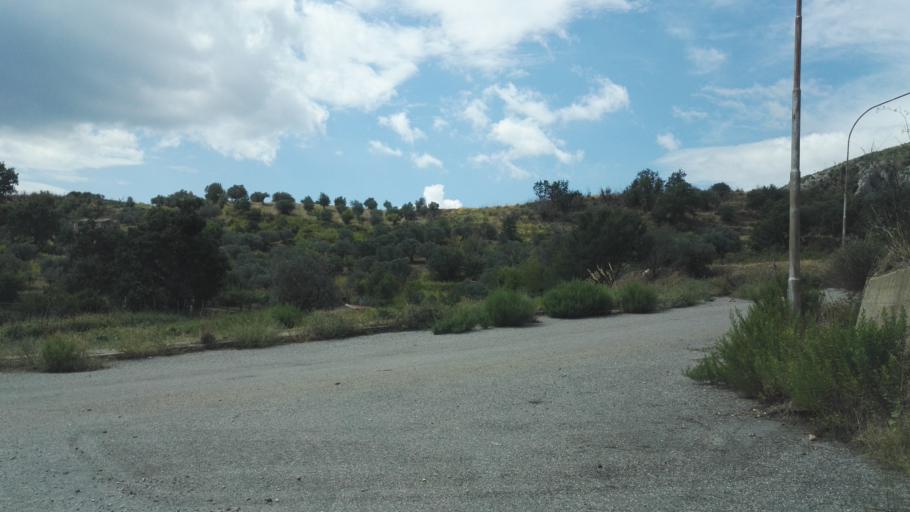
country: IT
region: Calabria
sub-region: Provincia di Reggio Calabria
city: Pazzano
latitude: 38.4642
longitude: 16.4524
